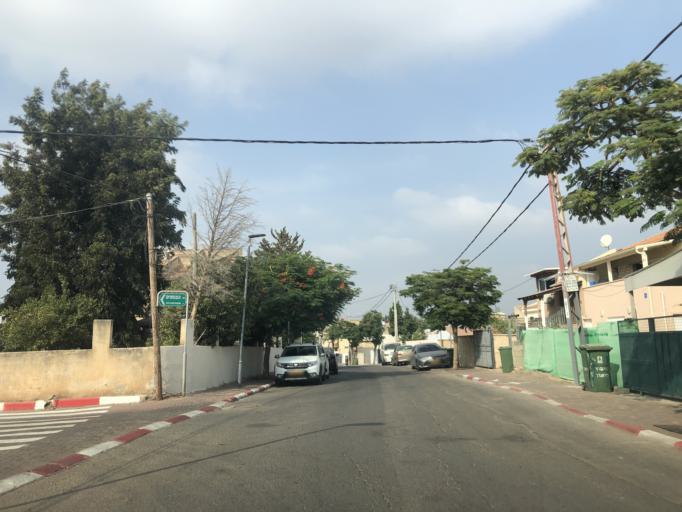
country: IL
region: Central District
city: Rosh Ha'Ayin
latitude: 32.0984
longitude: 34.9528
